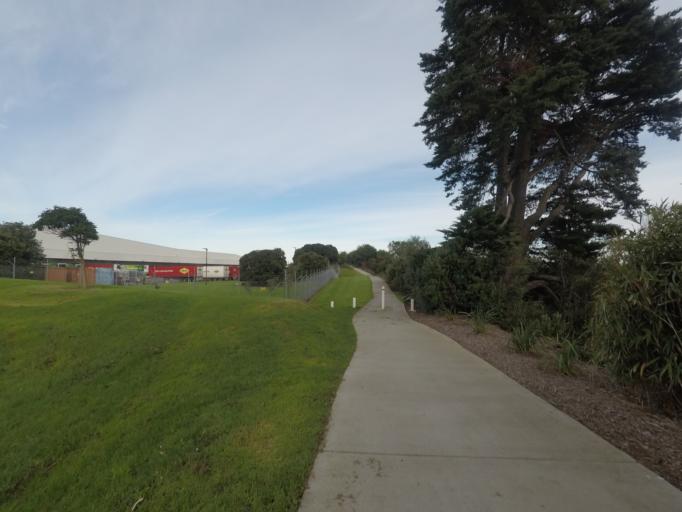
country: NZ
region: Auckland
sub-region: Auckland
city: Mangere
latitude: -36.9447
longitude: 174.8098
